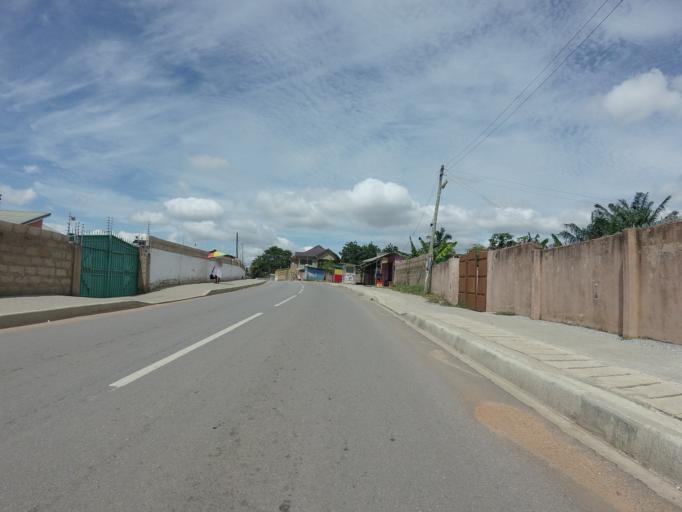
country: GH
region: Central
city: Kasoa
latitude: 5.5401
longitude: -0.4005
